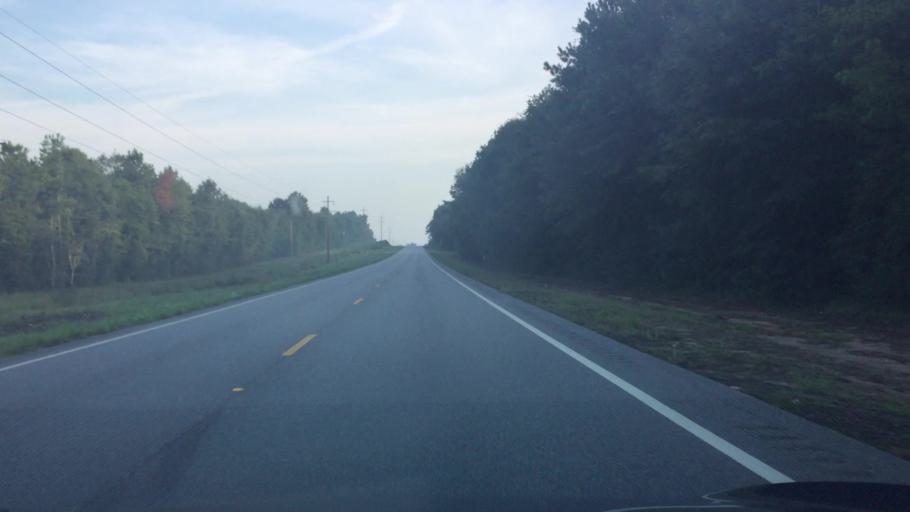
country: US
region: Alabama
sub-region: Covington County
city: Florala
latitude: 31.0654
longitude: -86.3991
